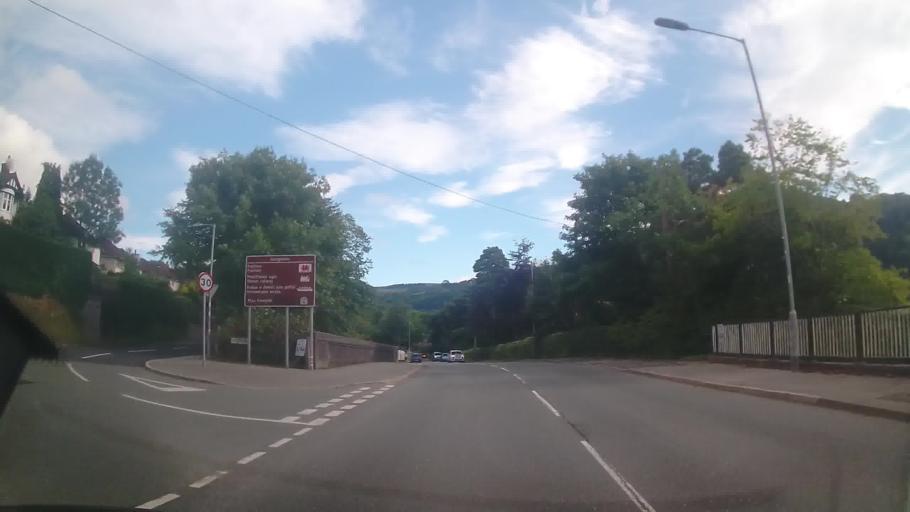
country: GB
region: Wales
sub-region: Denbighshire
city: Llangollen
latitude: 52.9791
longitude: -3.1783
